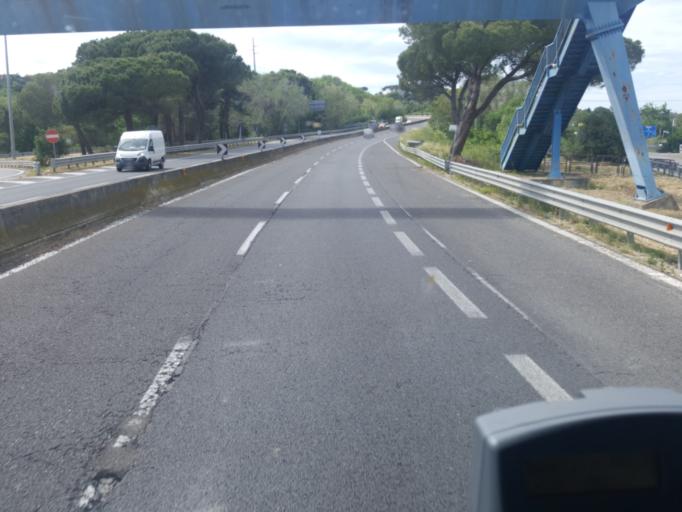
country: IT
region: Latium
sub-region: Citta metropolitana di Roma Capitale
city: Ara Nova
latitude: 41.9072
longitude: 12.2641
